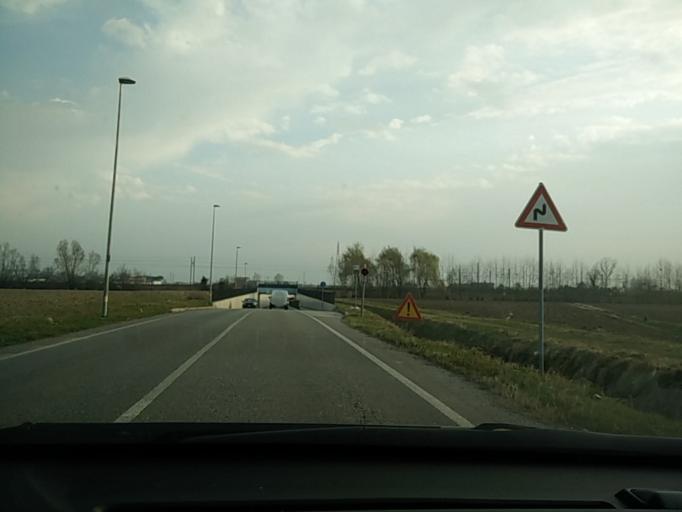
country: IT
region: Veneto
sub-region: Provincia di Venezia
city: Fossalta di Piave
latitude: 45.6266
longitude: 12.5044
